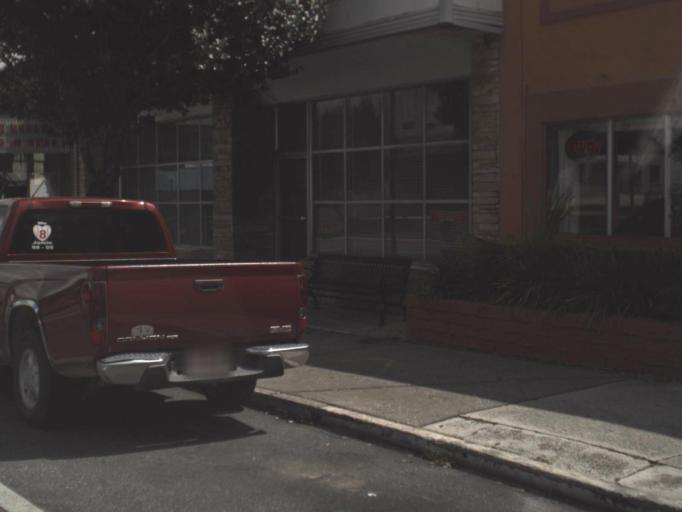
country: US
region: Florida
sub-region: Pasco County
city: Dade City
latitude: 28.3662
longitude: -82.1890
